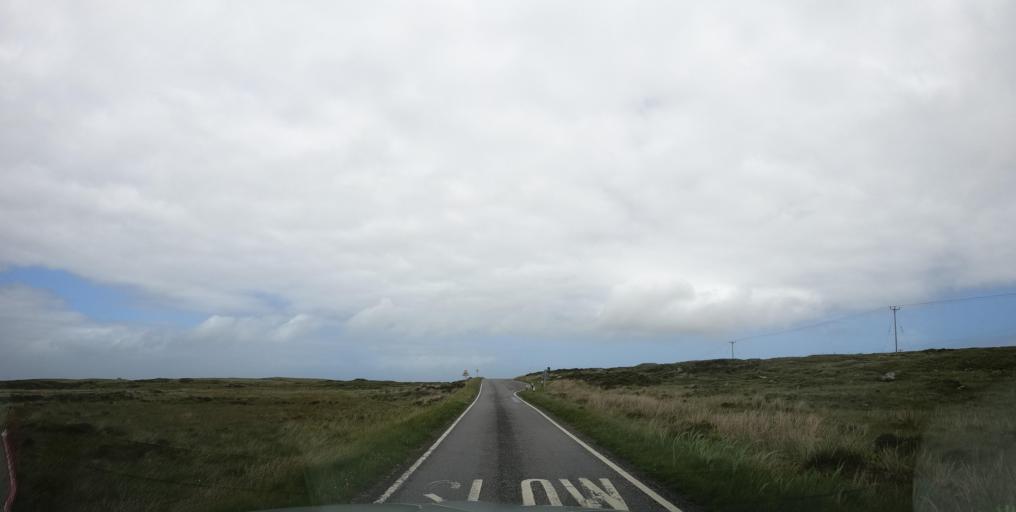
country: GB
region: Scotland
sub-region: Eilean Siar
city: Isle of South Uist
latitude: 57.2817
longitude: -7.3664
